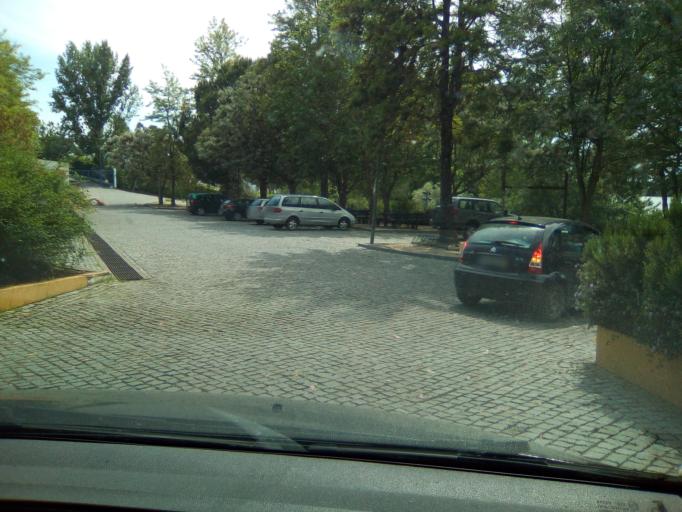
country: PT
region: Portalegre
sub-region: Avis
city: Avis
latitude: 39.0567
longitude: -7.9116
